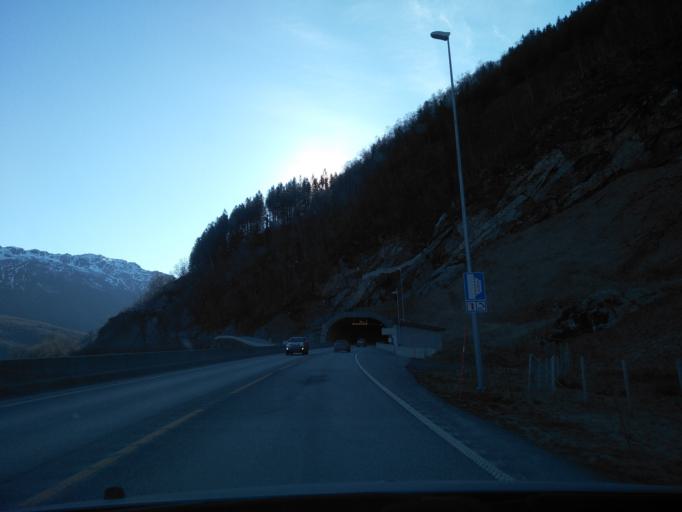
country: NO
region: Hordaland
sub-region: Etne
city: Etne
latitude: 59.7230
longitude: 6.1173
